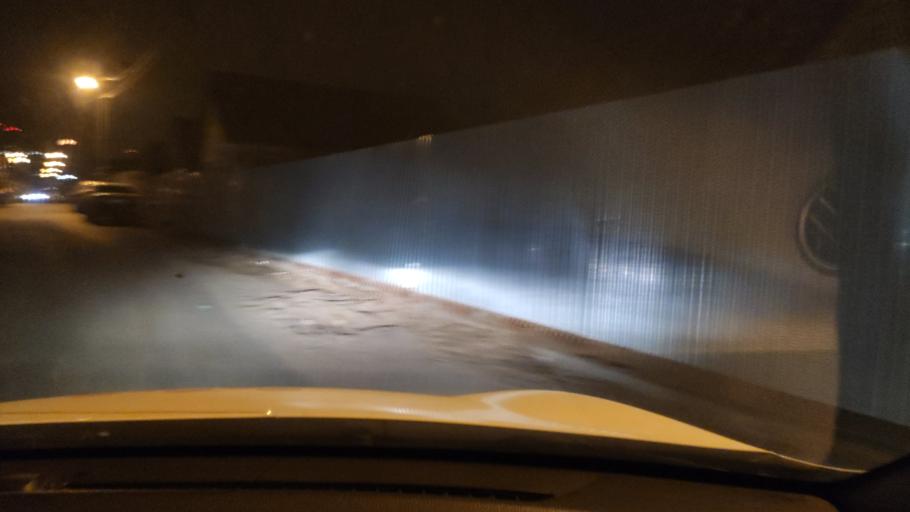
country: RU
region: Tatarstan
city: Osinovo
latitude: 55.8471
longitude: 48.8961
